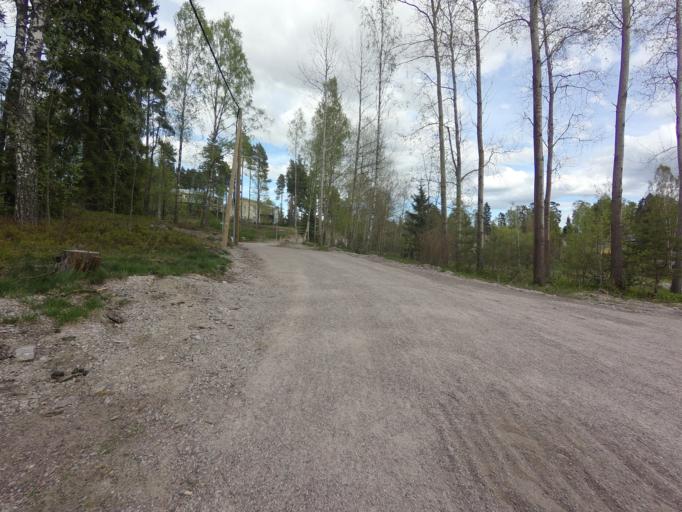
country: FI
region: Uusimaa
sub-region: Helsinki
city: Kauniainen
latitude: 60.1891
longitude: 24.7206
